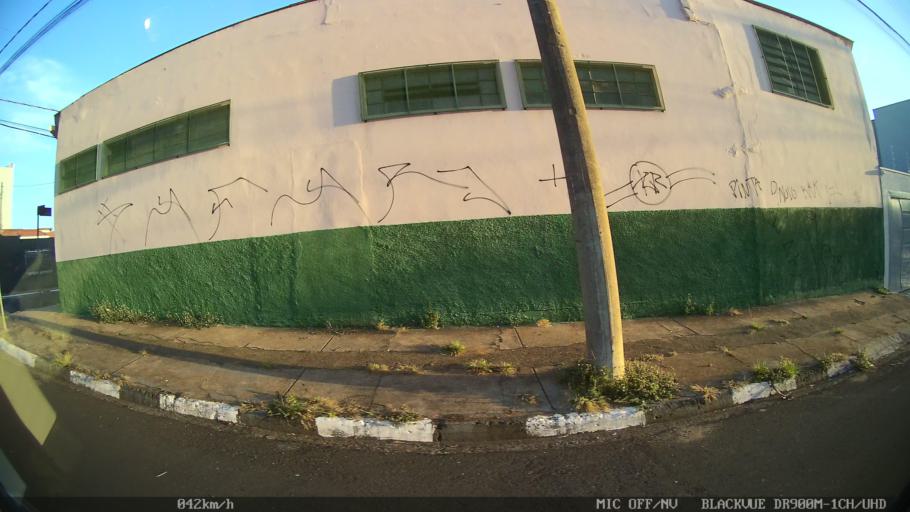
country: BR
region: Sao Paulo
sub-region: Franca
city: Franca
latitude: -20.5172
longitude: -47.4120
